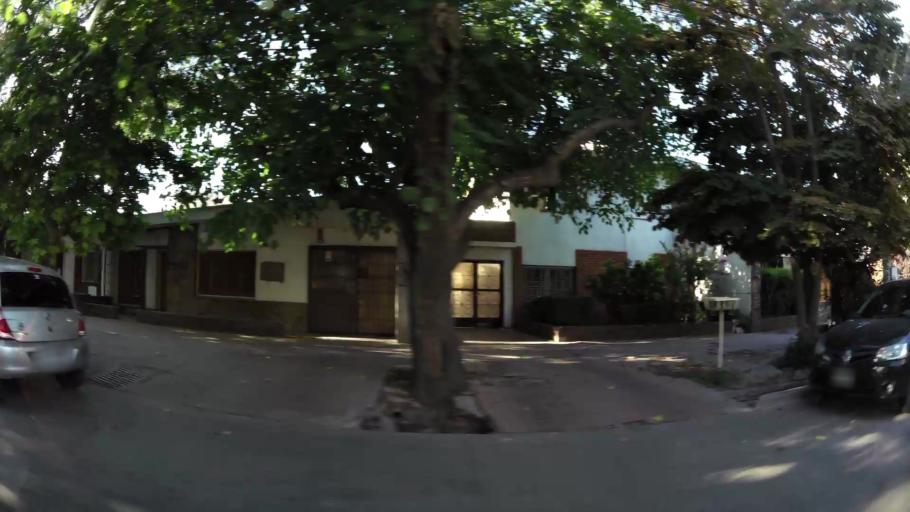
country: AR
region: Mendoza
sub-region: Departamento de Godoy Cruz
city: Godoy Cruz
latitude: -32.9125
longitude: -68.8411
